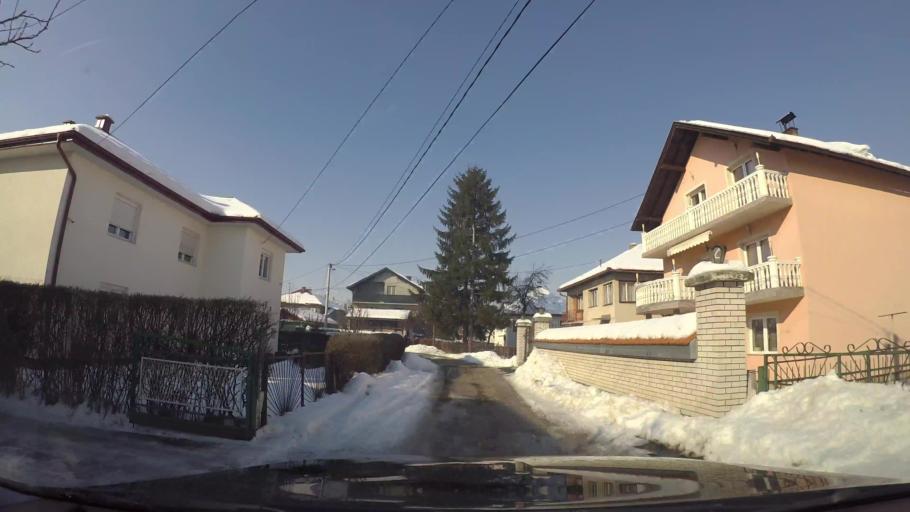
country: BA
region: Federation of Bosnia and Herzegovina
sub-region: Kanton Sarajevo
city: Sarajevo
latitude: 43.8141
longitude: 18.3146
